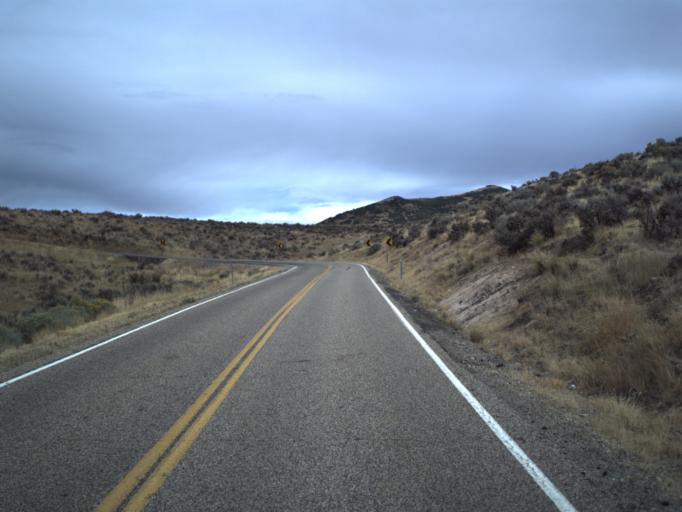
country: US
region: Utah
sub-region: Morgan County
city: Morgan
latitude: 40.9218
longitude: -111.5811
